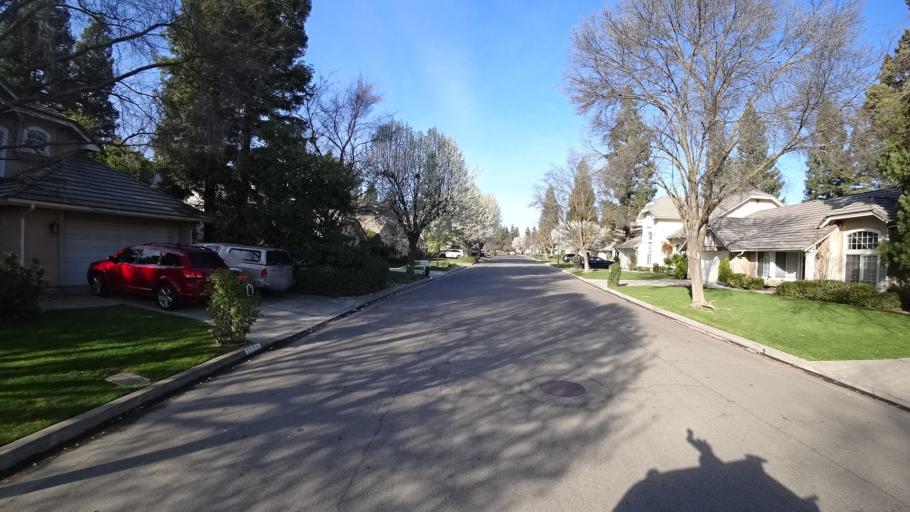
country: US
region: California
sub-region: Fresno County
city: Clovis
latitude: 36.8682
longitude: -119.7607
